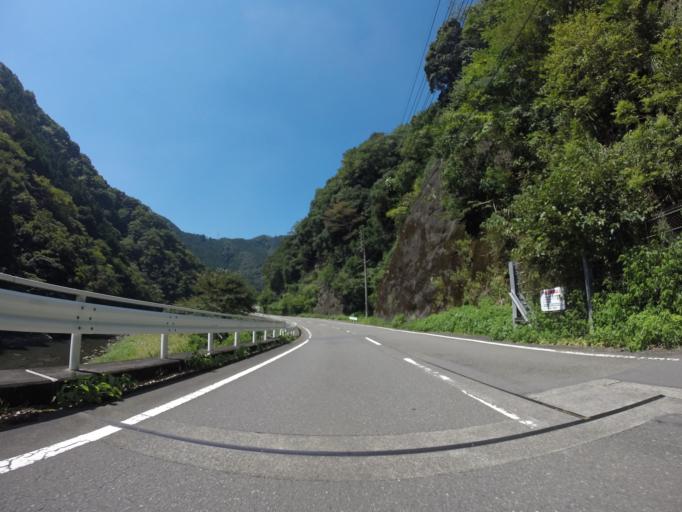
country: JP
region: Shizuoka
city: Shizuoka-shi
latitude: 35.0409
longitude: 138.2564
